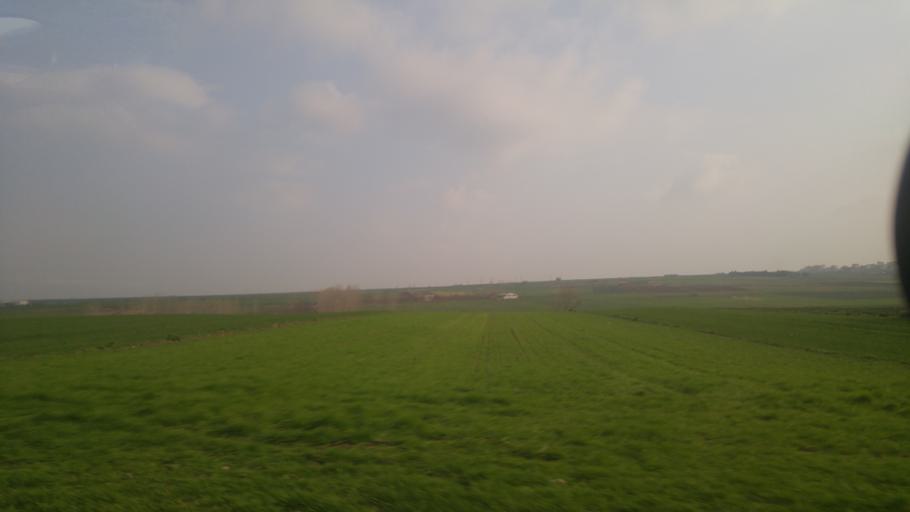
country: TR
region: Istanbul
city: Silivri
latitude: 41.0931
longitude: 28.2750
